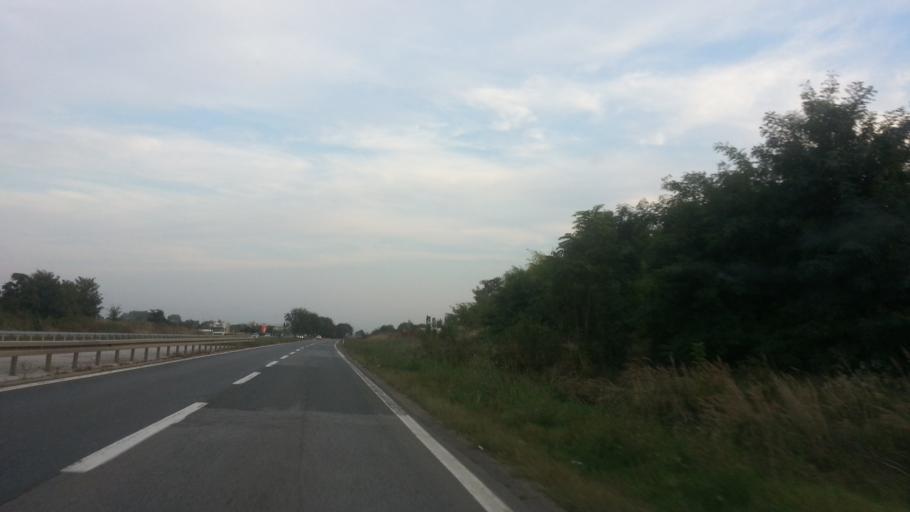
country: RS
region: Central Serbia
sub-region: Belgrade
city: Zemun
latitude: 44.8766
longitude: 20.3268
